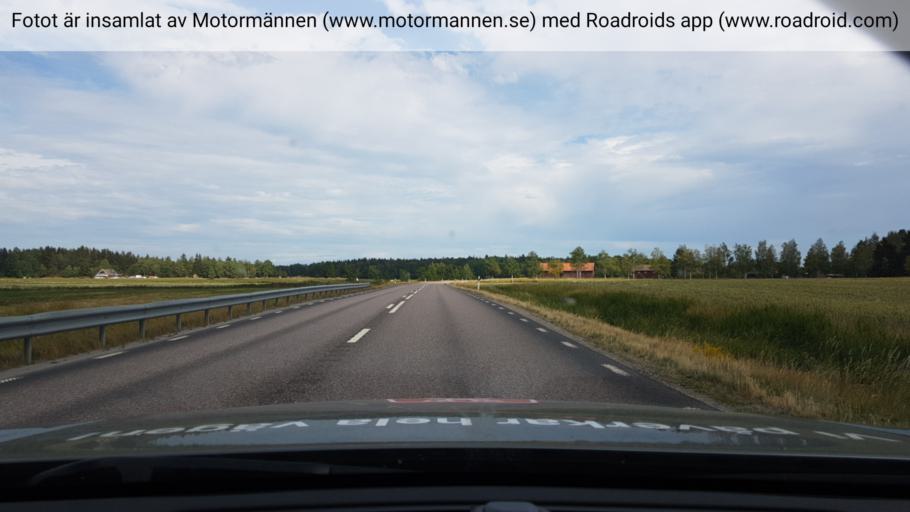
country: SE
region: Uppsala
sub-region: Enkopings Kommun
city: Orsundsbro
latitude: 59.8789
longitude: 17.2722
